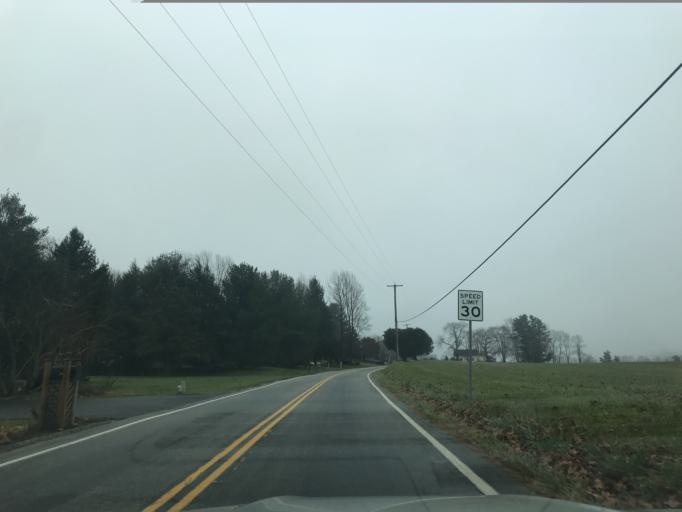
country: US
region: Maryland
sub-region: Harford County
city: South Bel Air
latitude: 39.5905
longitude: -76.2831
